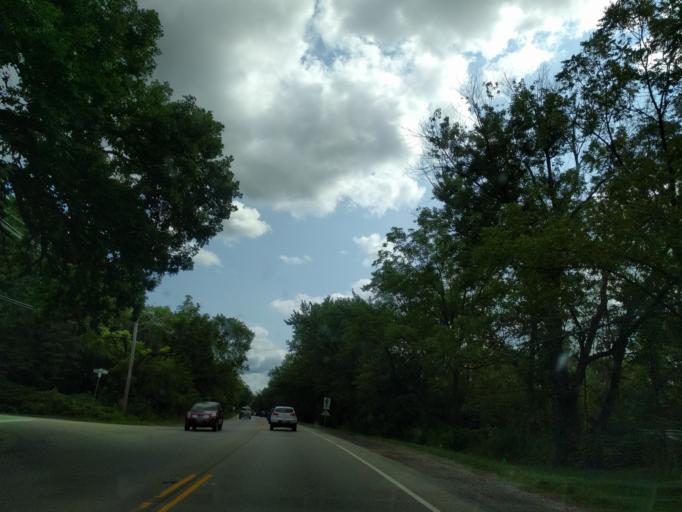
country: US
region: Illinois
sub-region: Lake County
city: Long Grove
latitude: 42.1703
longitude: -88.0162
